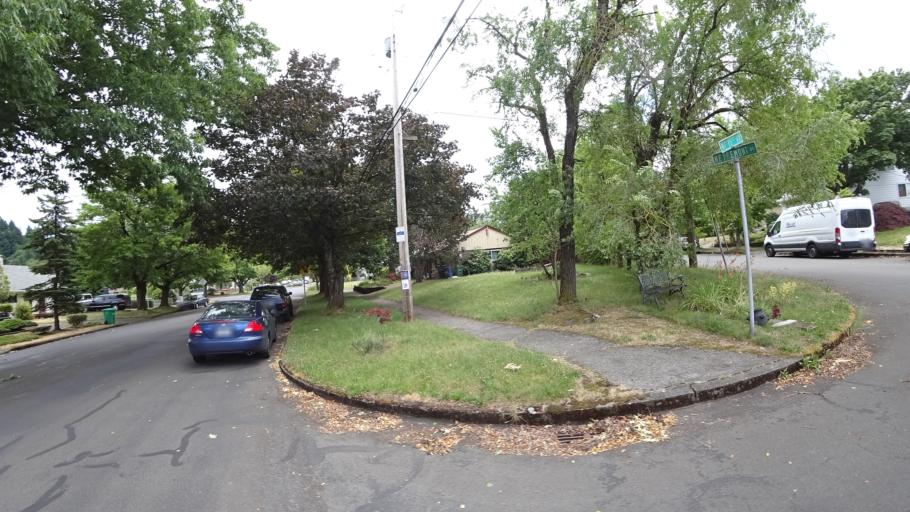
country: US
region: Oregon
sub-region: Multnomah County
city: Lents
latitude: 45.5465
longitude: -122.5757
